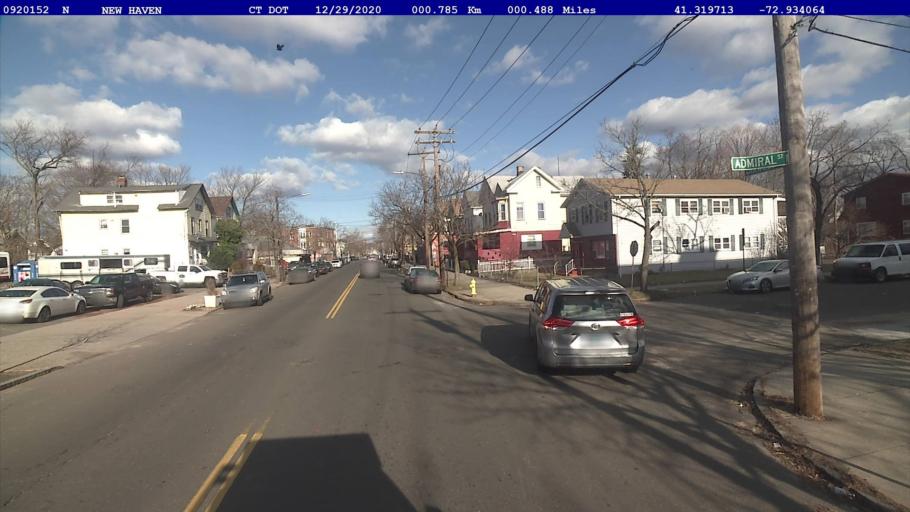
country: US
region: Connecticut
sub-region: New Haven County
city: New Haven
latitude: 41.3197
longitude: -72.9341
